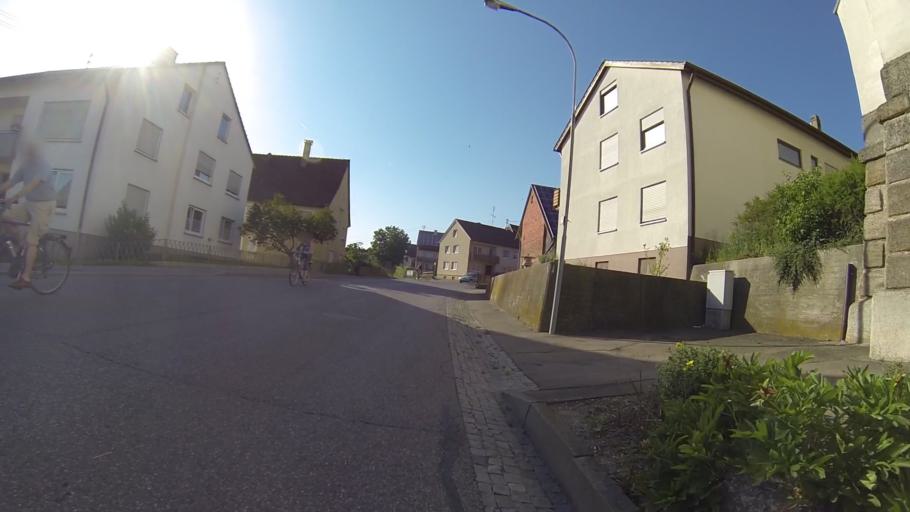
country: DE
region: Baden-Wuerttemberg
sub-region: Tuebingen Region
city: Mietingen
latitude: 48.1746
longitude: 9.8638
